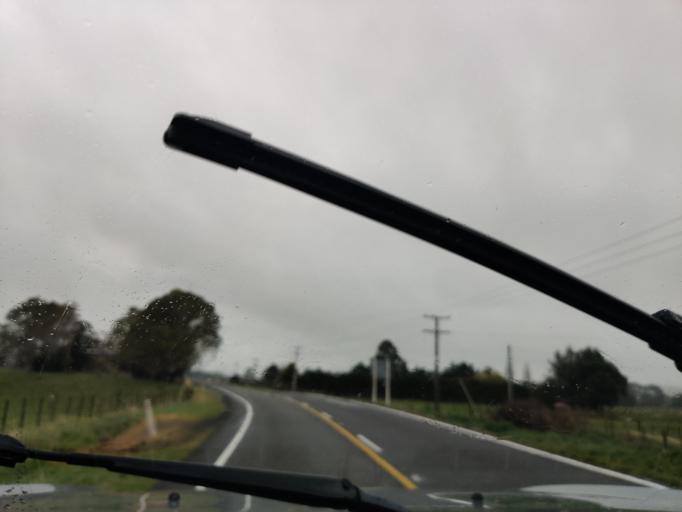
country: NZ
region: Hawke's Bay
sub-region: Hastings District
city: Hastings
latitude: -40.0215
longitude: 176.3306
